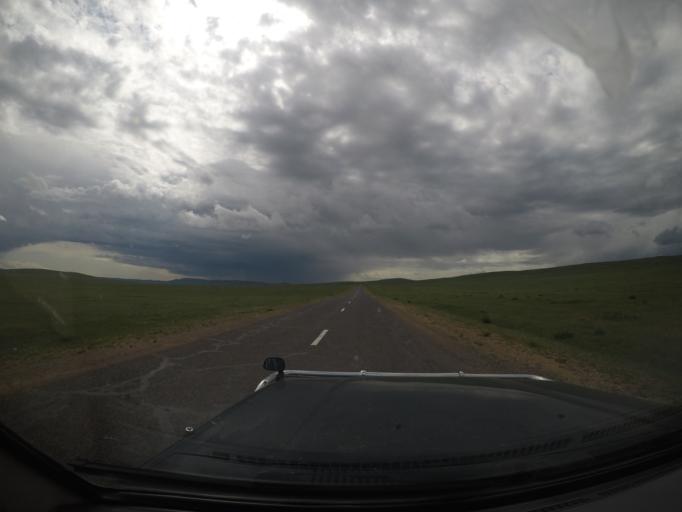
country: MN
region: Hentiy
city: Avraga
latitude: 47.4657
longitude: 109.5745
